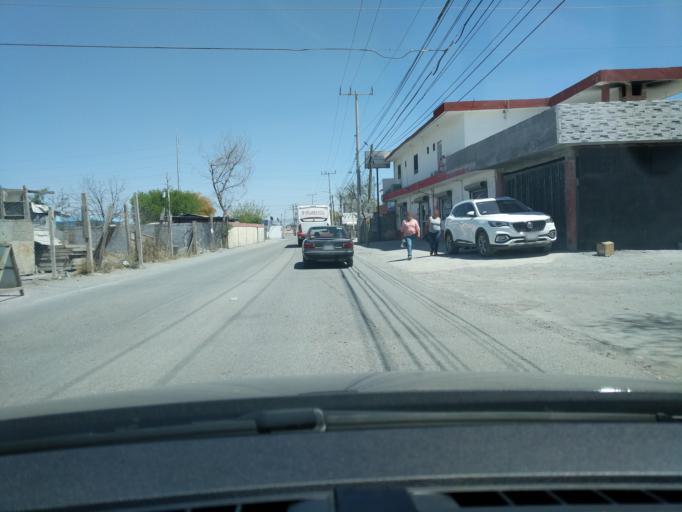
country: MX
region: Nuevo Leon
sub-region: Salinas Victoria
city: Emiliano Zapata
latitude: 25.9100
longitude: -100.2687
